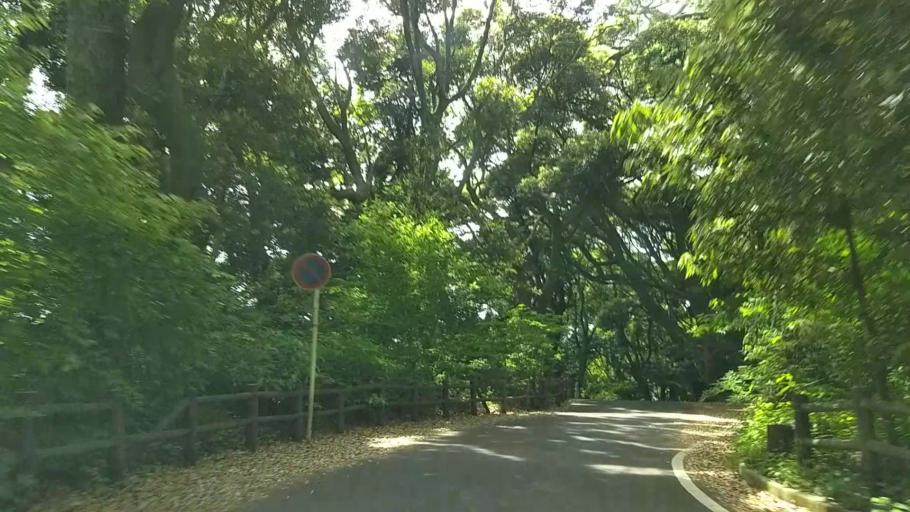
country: JP
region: Kanagawa
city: Yugawara
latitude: 35.1449
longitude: 139.1574
